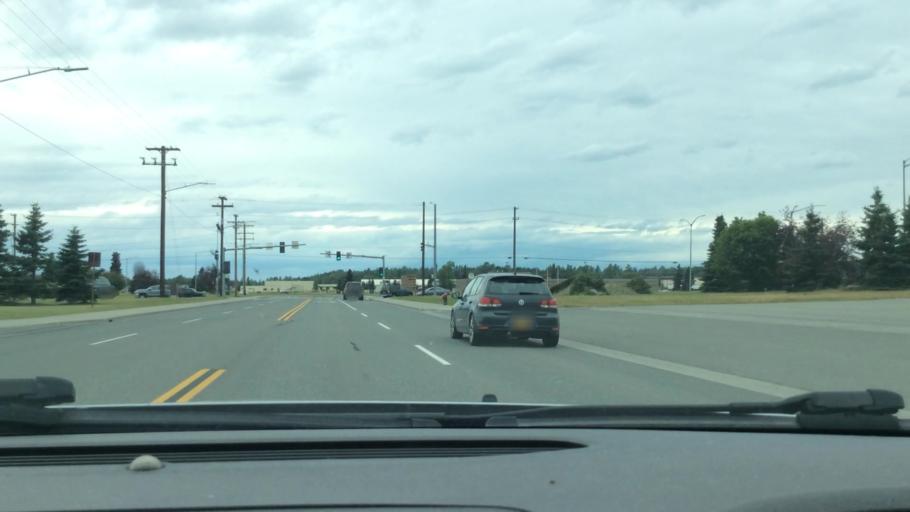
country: US
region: Alaska
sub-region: Anchorage Municipality
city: Anchorage
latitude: 61.2373
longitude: -149.8470
